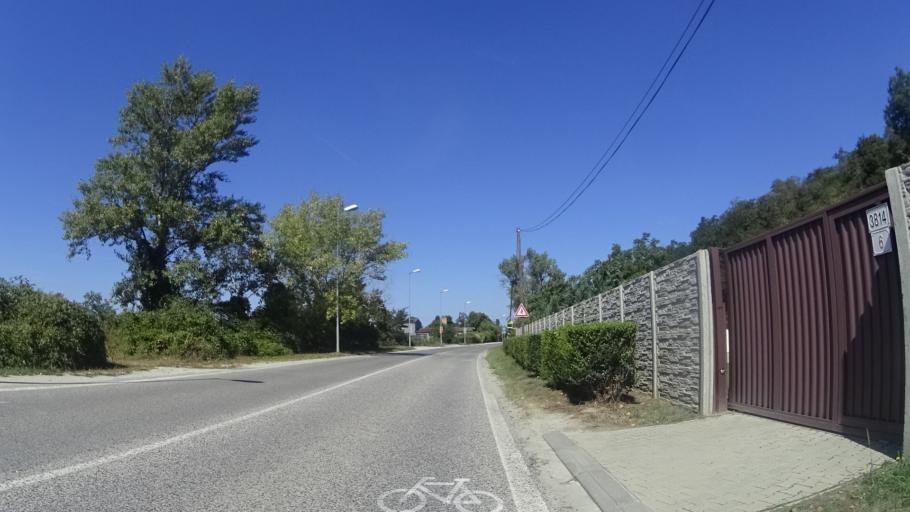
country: AT
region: Lower Austria
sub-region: Politischer Bezirk Bruck an der Leitha
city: Wolfsthal
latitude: 48.1579
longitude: 17.0093
